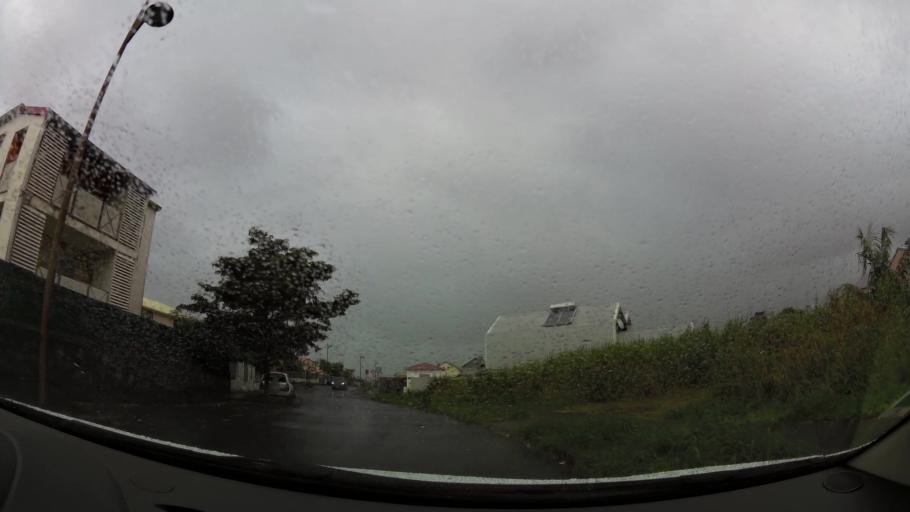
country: RE
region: Reunion
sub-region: Reunion
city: Saint-Andre
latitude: -20.9739
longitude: 55.6556
